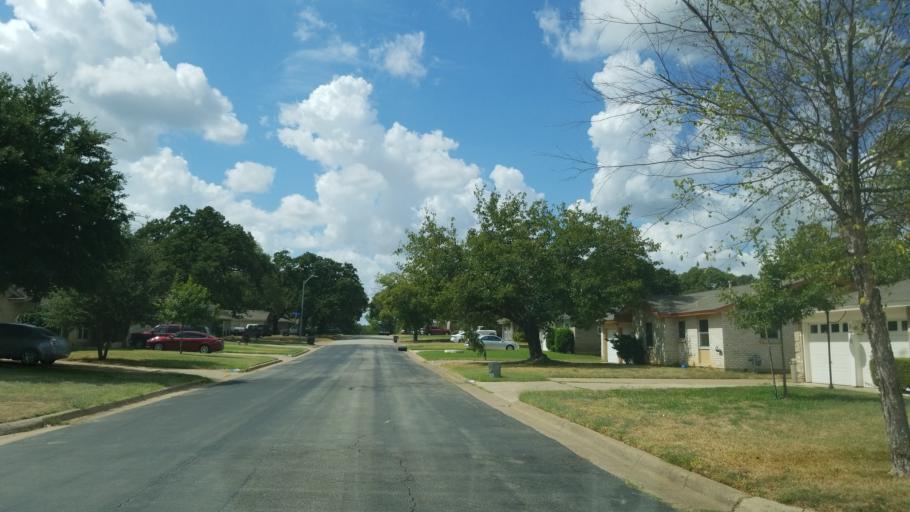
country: US
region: Texas
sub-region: Tarrant County
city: Euless
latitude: 32.8586
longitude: -97.0921
